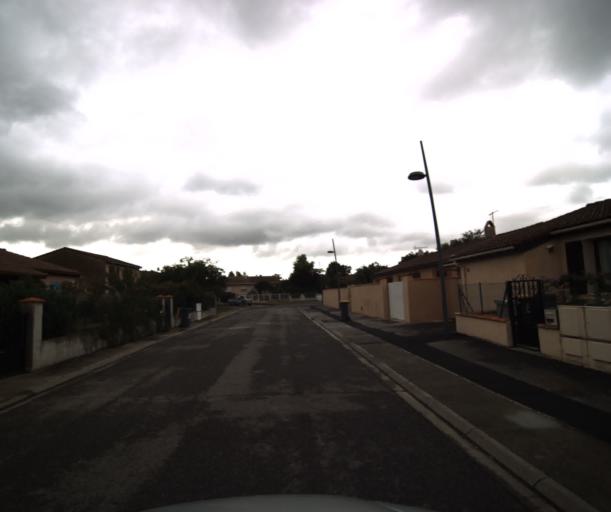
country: FR
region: Midi-Pyrenees
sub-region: Departement de la Haute-Garonne
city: Portet-sur-Garonne
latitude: 43.5439
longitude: 1.4133
